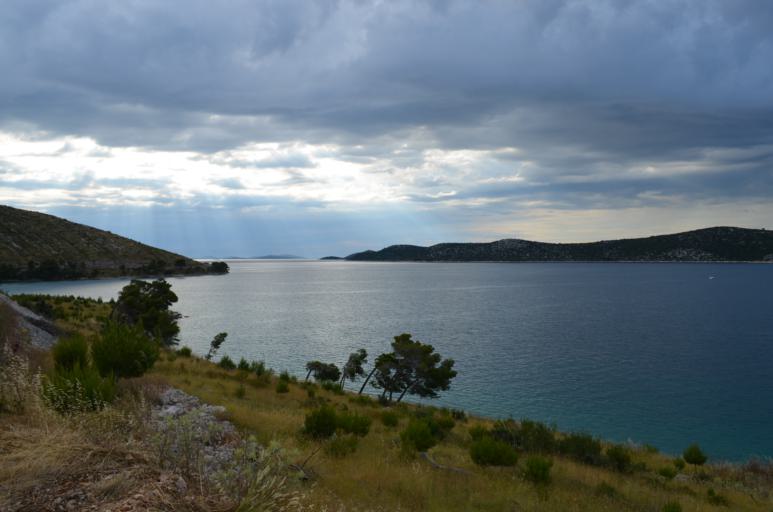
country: HR
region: Sibensko-Kniniska
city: Primosten
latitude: 43.6300
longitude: 15.9371
